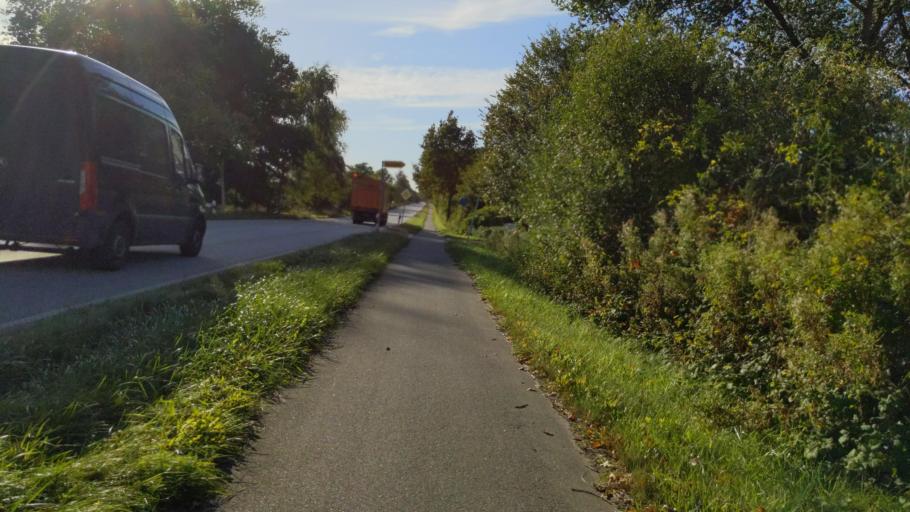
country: DE
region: Schleswig-Holstein
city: Ahrensbok
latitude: 54.0385
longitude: 10.6333
